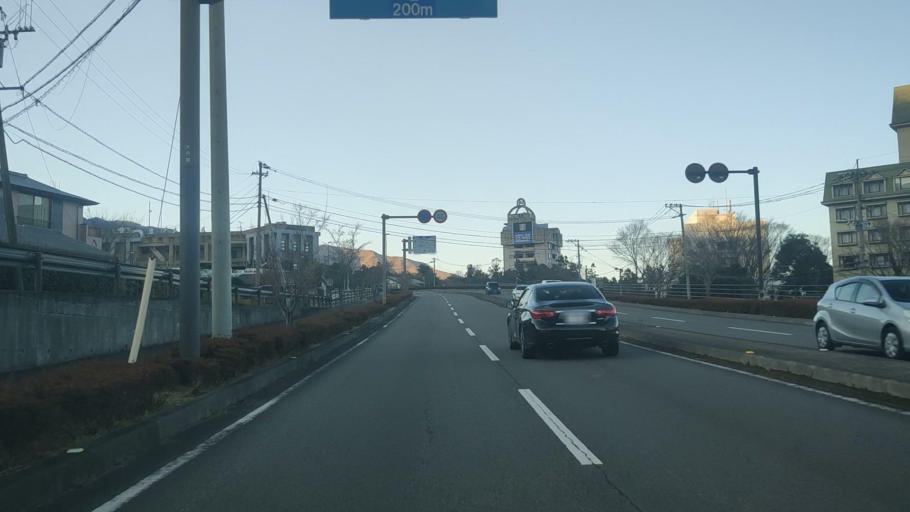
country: JP
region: Oita
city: Beppu
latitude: 33.2893
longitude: 131.4610
